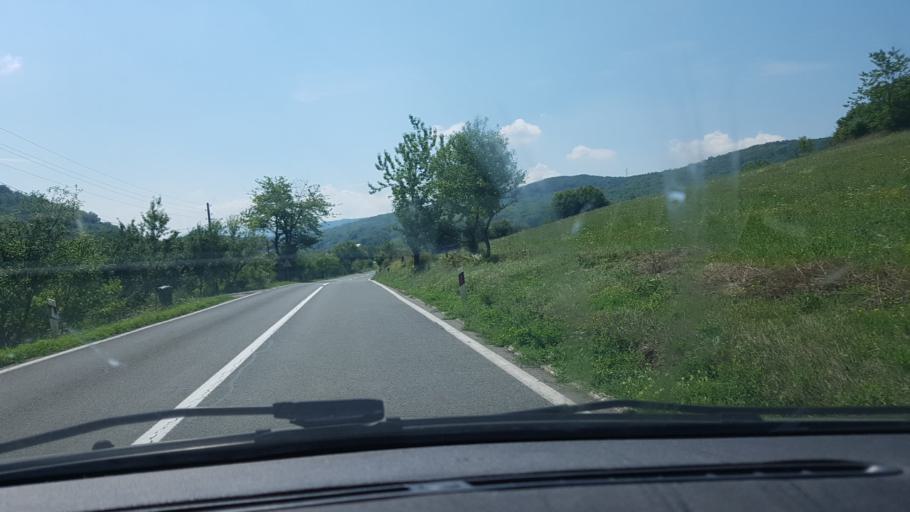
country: HR
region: Licko-Senjska
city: Otocac
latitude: 44.8896
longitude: 15.1914
